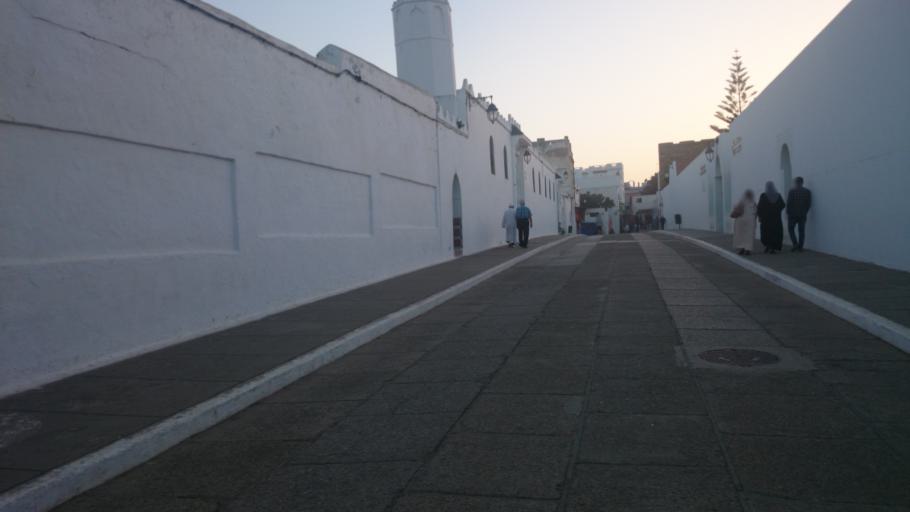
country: MA
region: Tanger-Tetouan
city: Asilah
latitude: 35.4666
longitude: -6.0367
